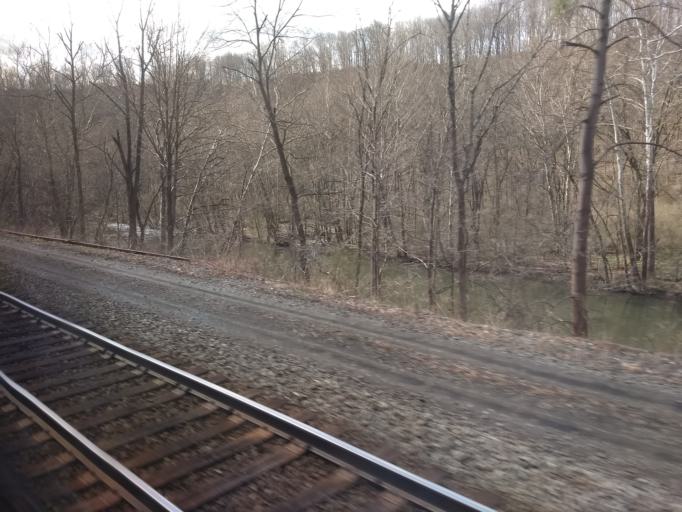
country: US
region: Pennsylvania
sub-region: Blair County
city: Tyrone
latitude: 40.6298
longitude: -78.1821
